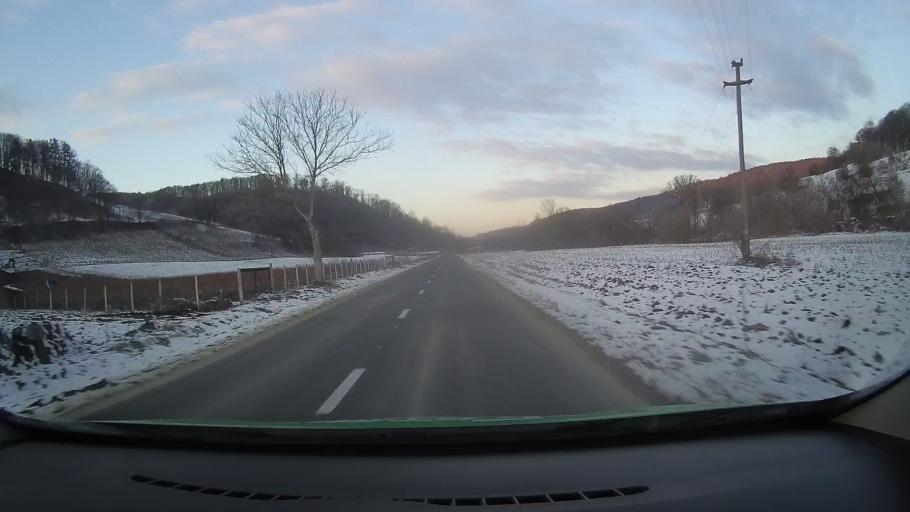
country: RO
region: Sibiu
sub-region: Comuna Atel
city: Atel
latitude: 46.1698
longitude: 24.4684
